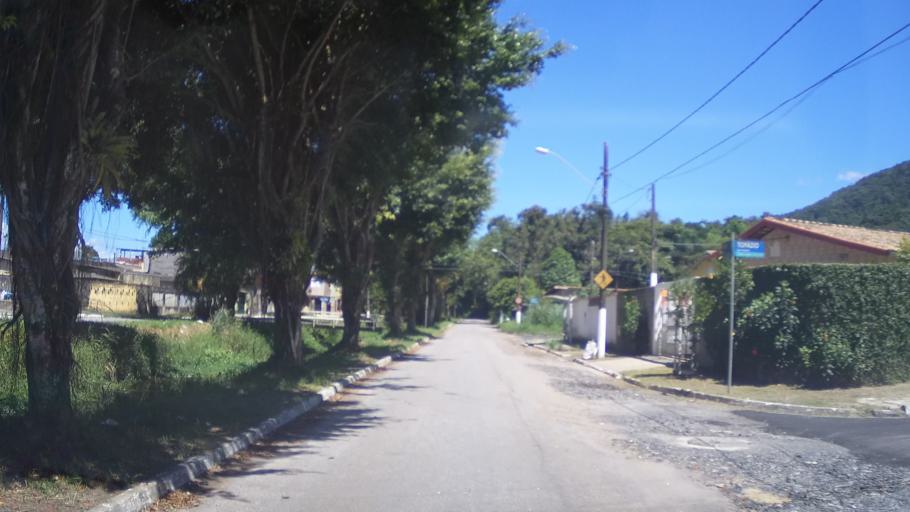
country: BR
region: Sao Paulo
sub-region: Mongagua
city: Mongagua
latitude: -24.0770
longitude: -46.5951
